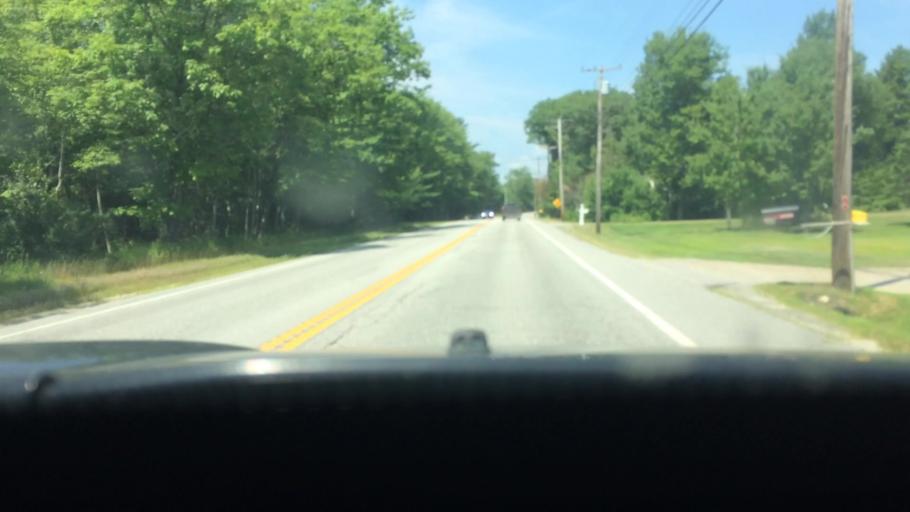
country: US
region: Maine
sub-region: Androscoggin County
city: Minot
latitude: 44.0888
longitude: -70.3391
